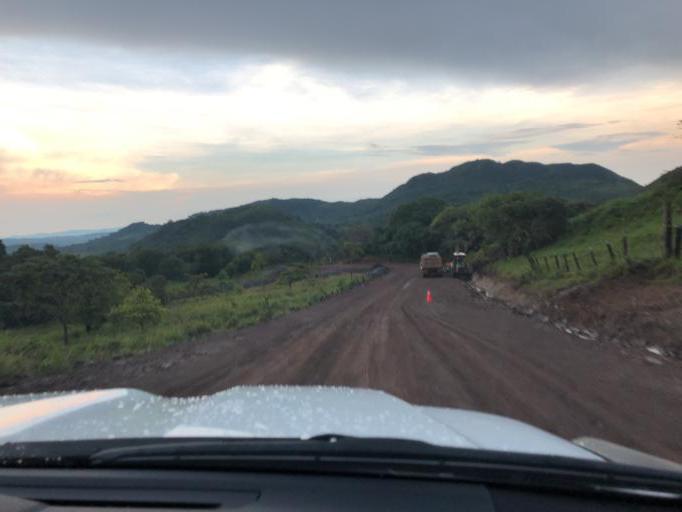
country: NI
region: Chontales
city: La Libertad
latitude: 12.1840
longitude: -85.1737
